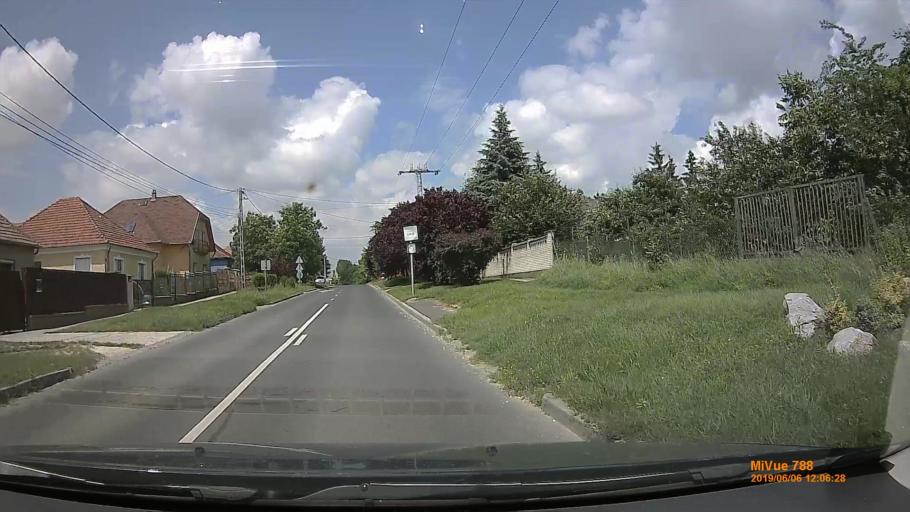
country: HU
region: Pest
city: Kerepes
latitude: 47.5623
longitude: 19.2795
